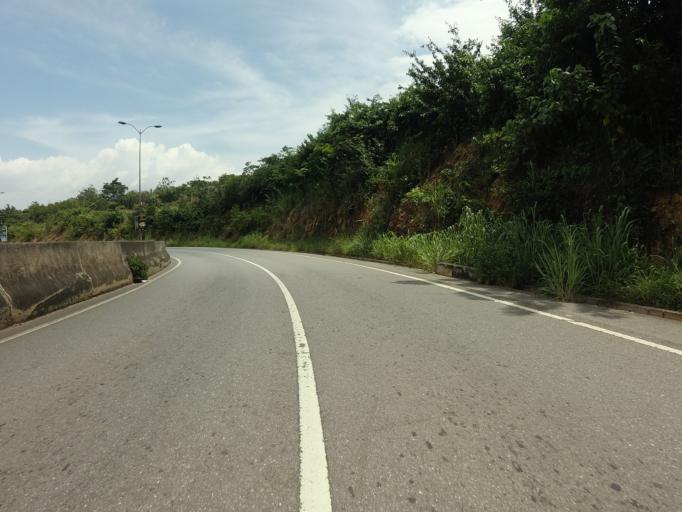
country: GH
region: Eastern
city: Aburi
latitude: 5.7994
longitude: -0.1849
